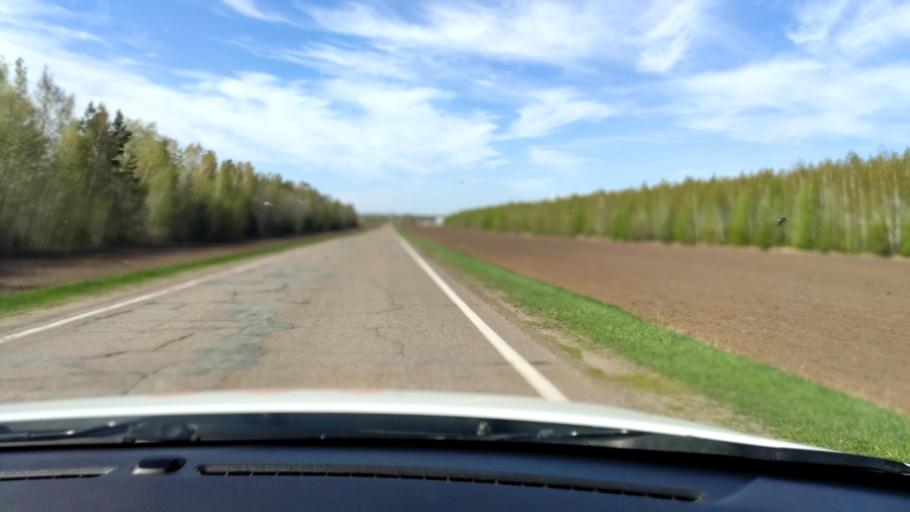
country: RU
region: Tatarstan
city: Stolbishchi
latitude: 55.5375
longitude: 49.2159
